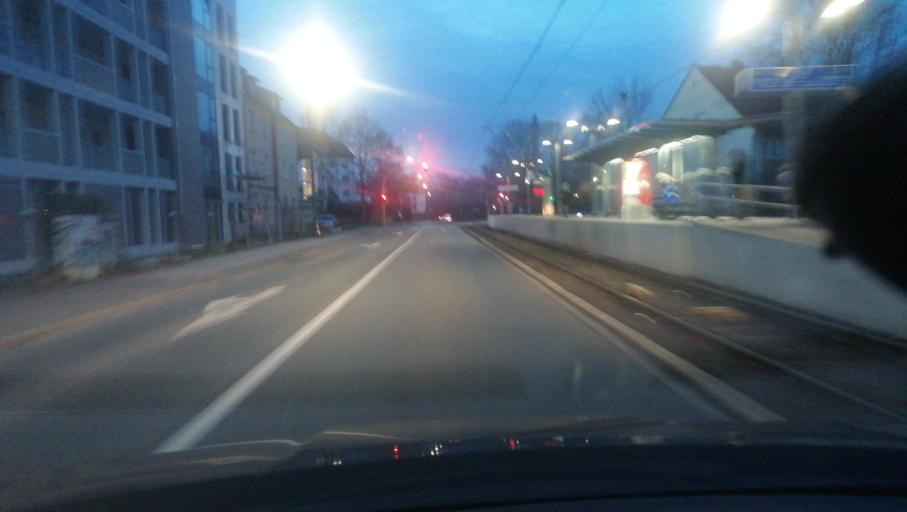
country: DE
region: North Rhine-Westphalia
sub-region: Regierungsbezirk Arnsberg
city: Dortmund
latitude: 51.5316
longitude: 7.4186
